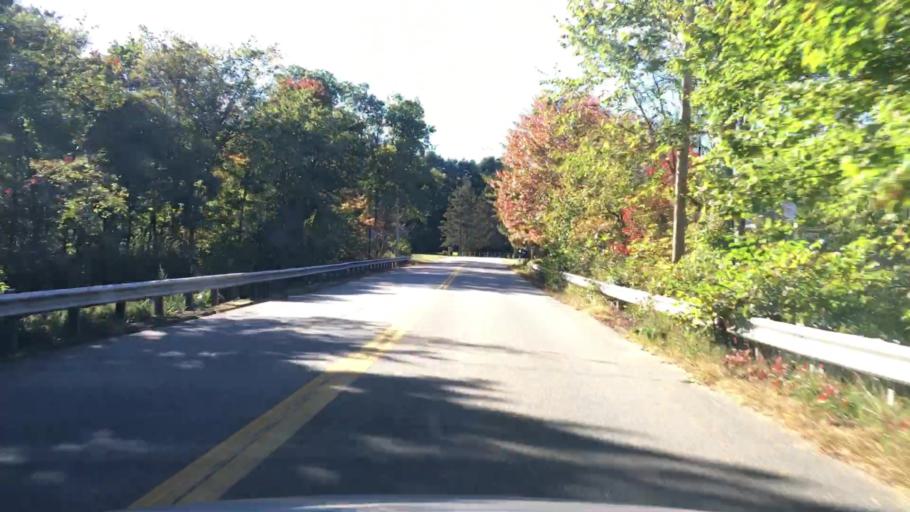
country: US
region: Maine
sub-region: Androscoggin County
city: Lisbon
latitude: 44.0721
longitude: -70.1405
